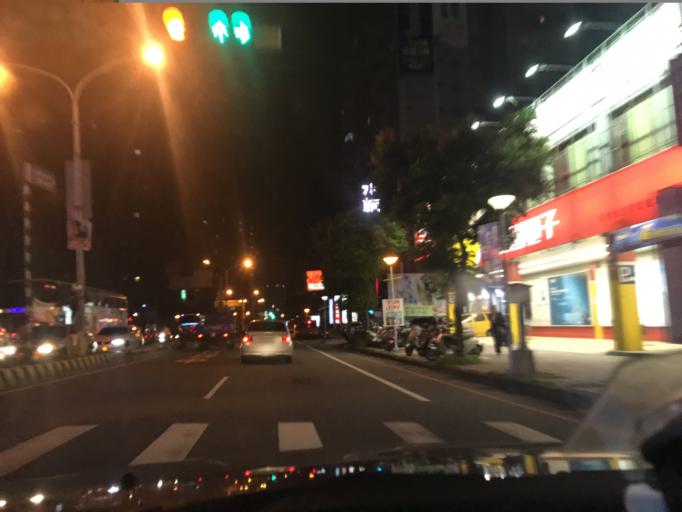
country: TW
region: Taiwan
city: Daxi
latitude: 24.9403
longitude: 121.2164
